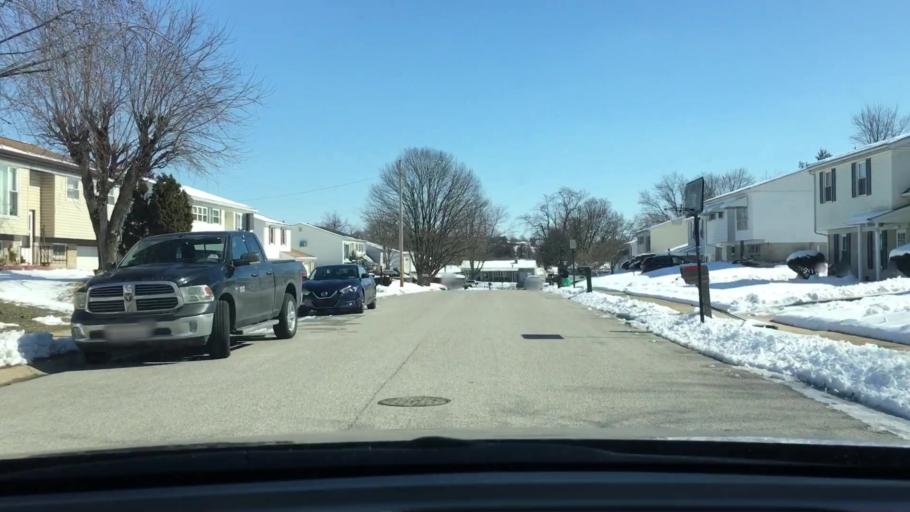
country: US
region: Pennsylvania
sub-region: York County
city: North York
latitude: 39.9784
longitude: -76.7539
